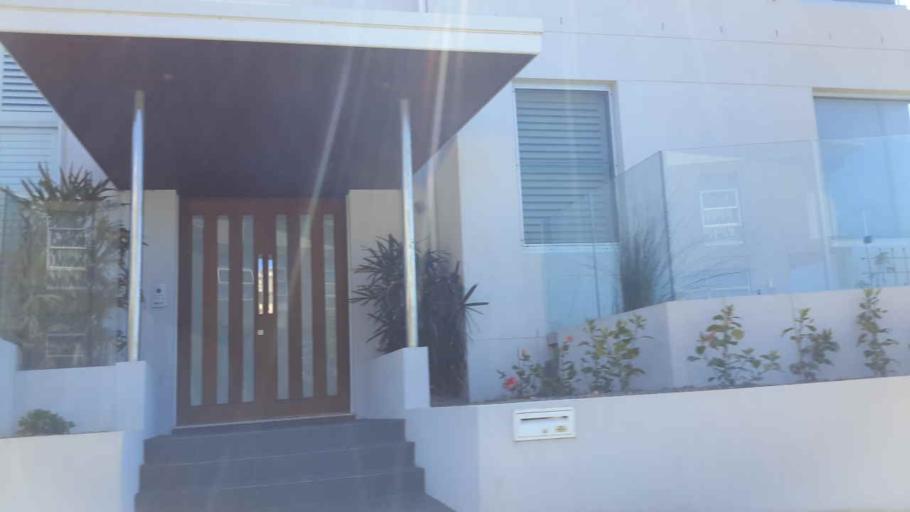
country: AU
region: New South Wales
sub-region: Wollongong
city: Bulli
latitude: -34.3282
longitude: 150.9237
